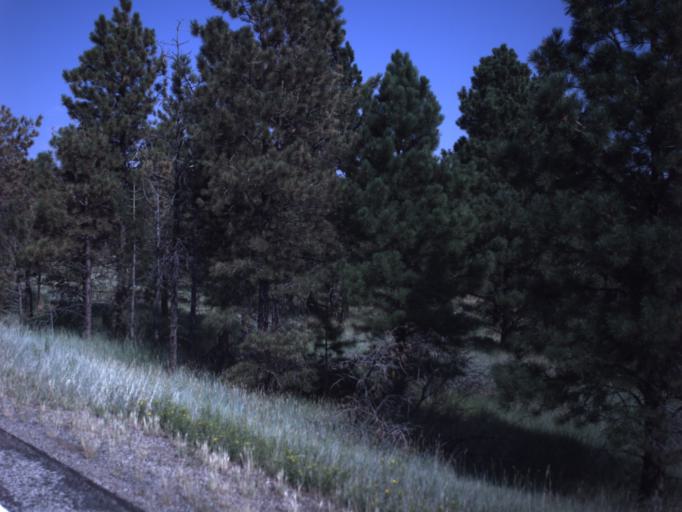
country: US
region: Utah
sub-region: Daggett County
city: Manila
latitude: 40.8704
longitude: -109.5032
